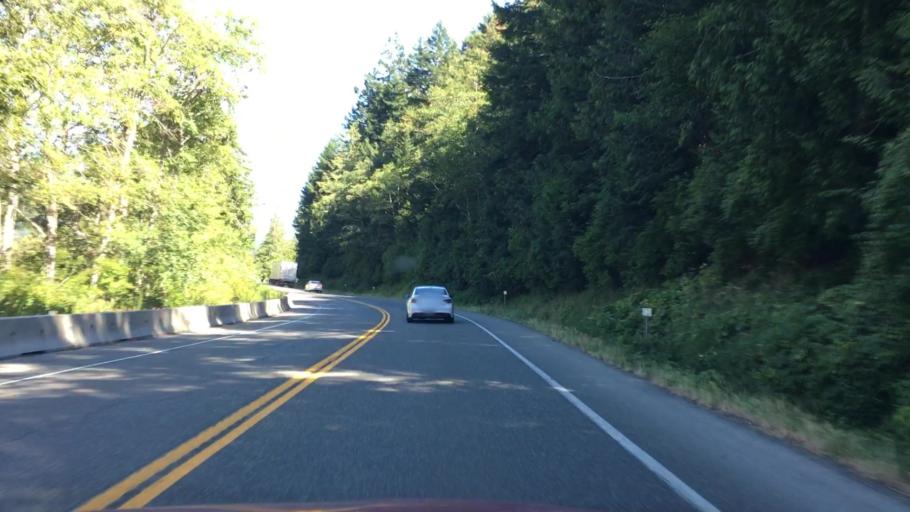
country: CA
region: British Columbia
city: Port Alberni
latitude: 49.2899
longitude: -124.6471
